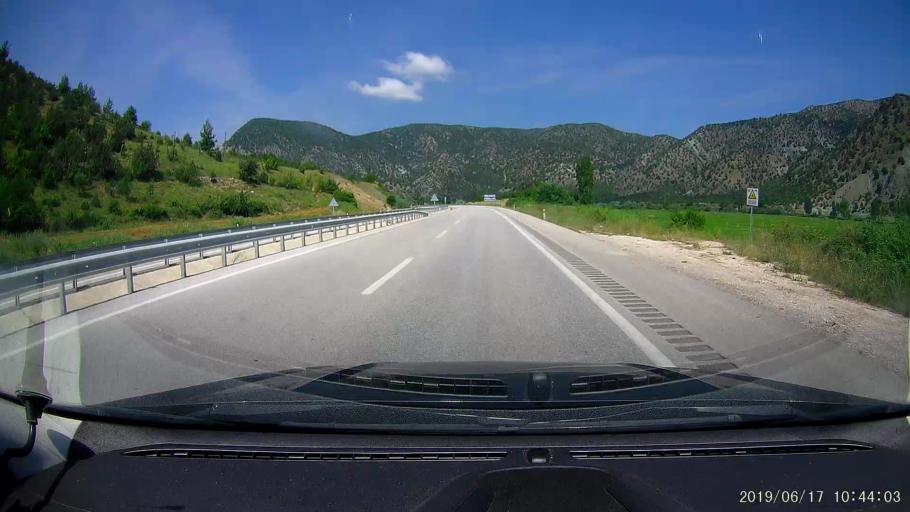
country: TR
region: Corum
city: Kargi
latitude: 41.0713
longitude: 34.5219
